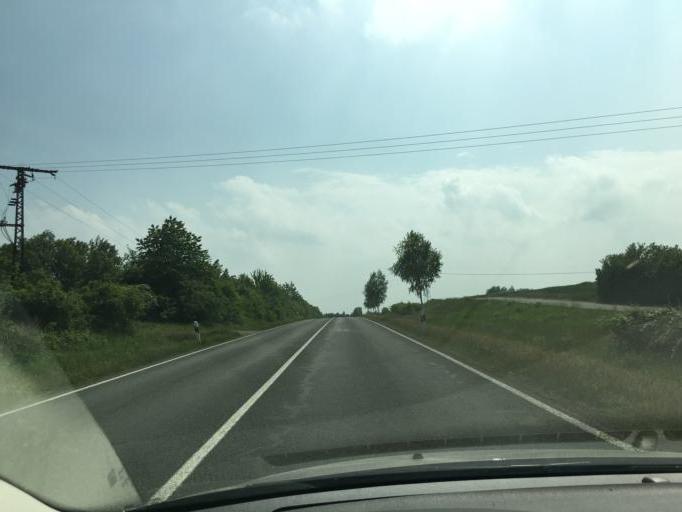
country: DE
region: Saxony
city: Grossbothen
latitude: 51.1590
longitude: 12.7636
